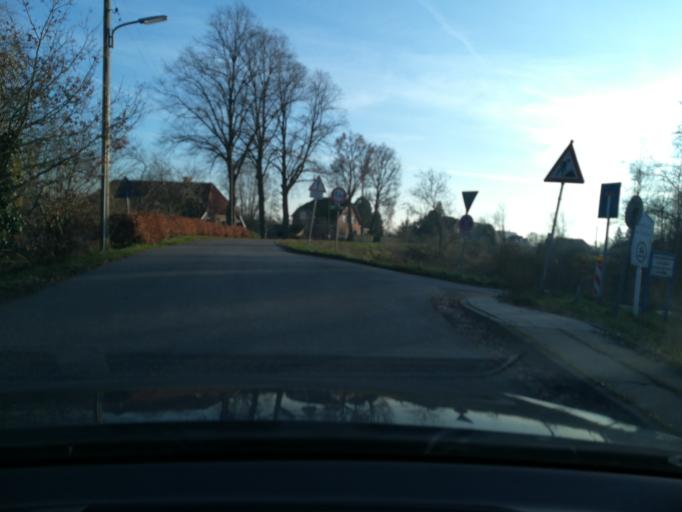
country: DE
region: Lower Saxony
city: Stelle
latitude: 53.4403
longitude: 10.1204
